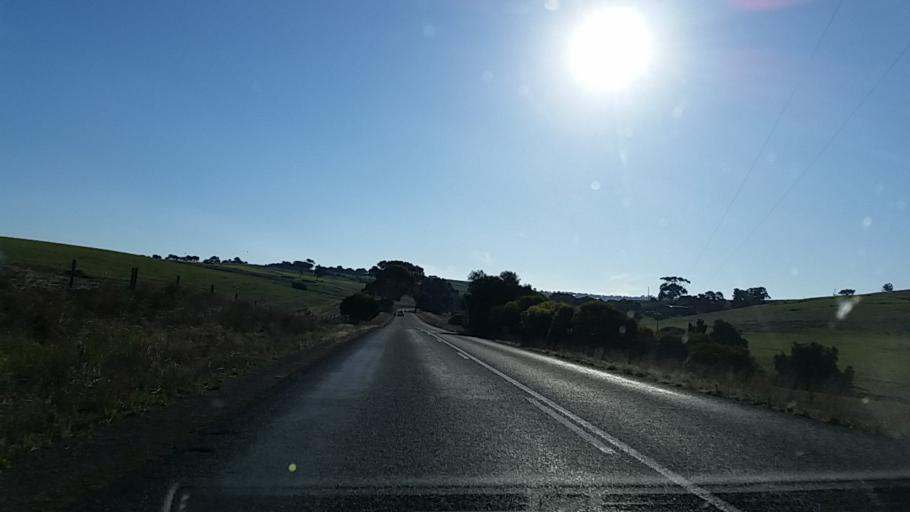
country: AU
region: South Australia
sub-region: Alexandrina
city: Strathalbyn
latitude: -35.1874
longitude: 138.9555
